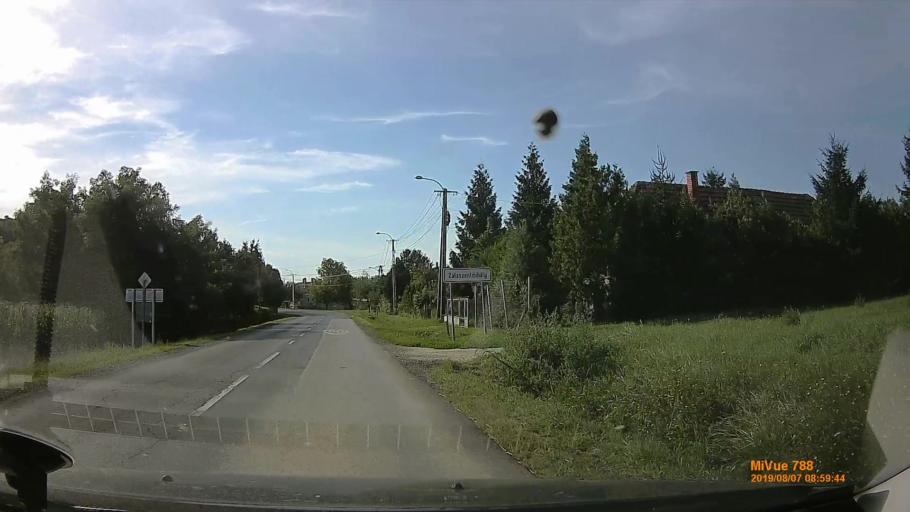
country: HU
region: Zala
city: Pacsa
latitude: 46.7319
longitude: 16.9407
